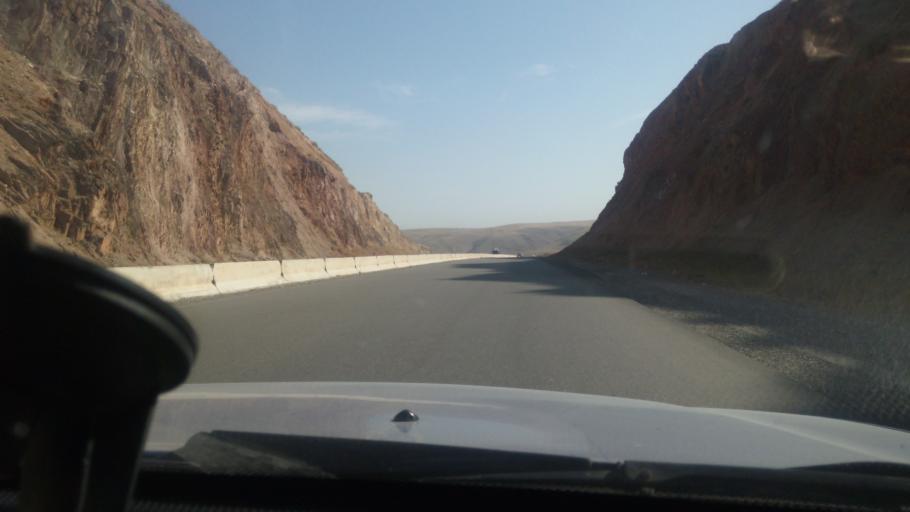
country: UZ
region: Jizzax
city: Jizzax
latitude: 40.0499
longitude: 67.6802
